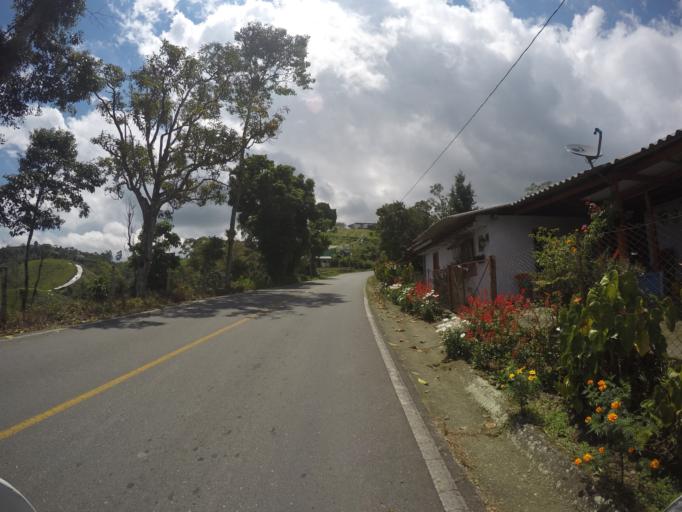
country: CO
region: Quindio
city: Filandia
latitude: 4.6527
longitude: -75.6777
